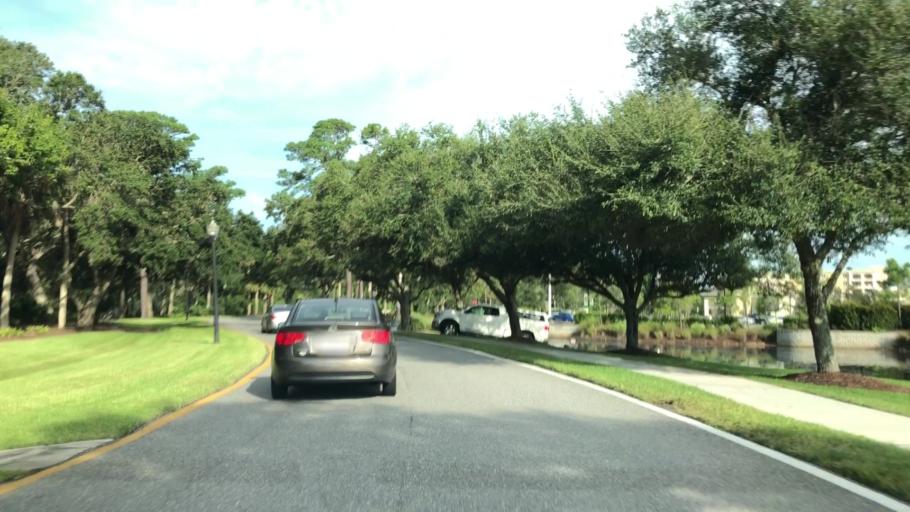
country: US
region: Florida
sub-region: Saint Johns County
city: Sawgrass
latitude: 30.2030
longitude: -81.3810
